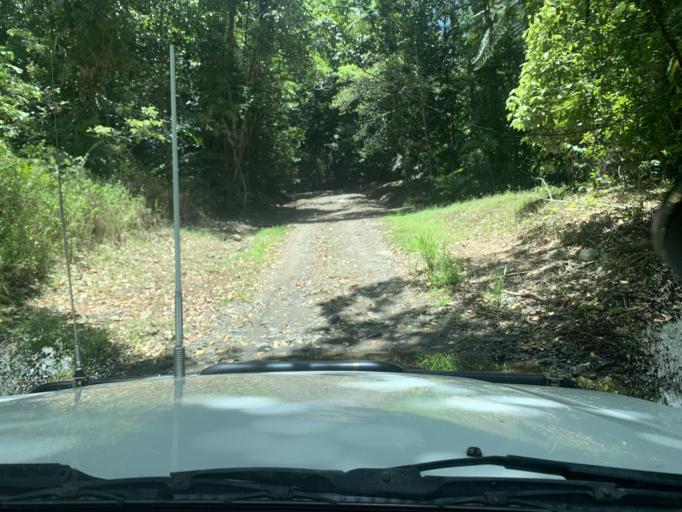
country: AU
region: Queensland
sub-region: Cairns
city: Redlynch
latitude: -16.9664
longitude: 145.6483
